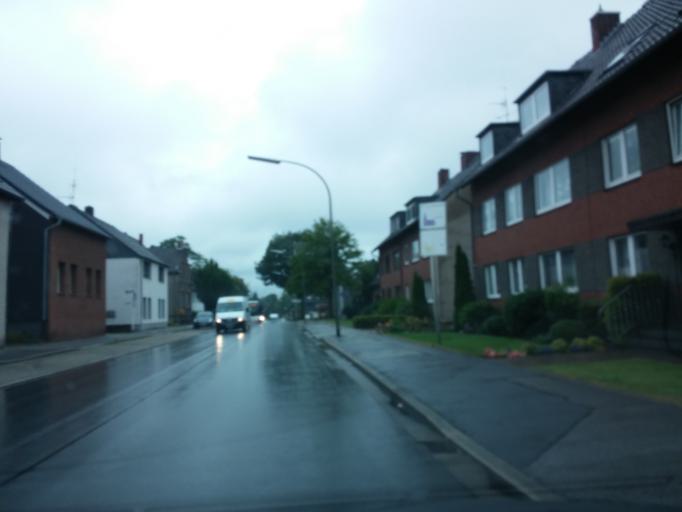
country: DE
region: North Rhine-Westphalia
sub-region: Regierungsbezirk Munster
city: Gladbeck
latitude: 51.5801
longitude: 7.0210
